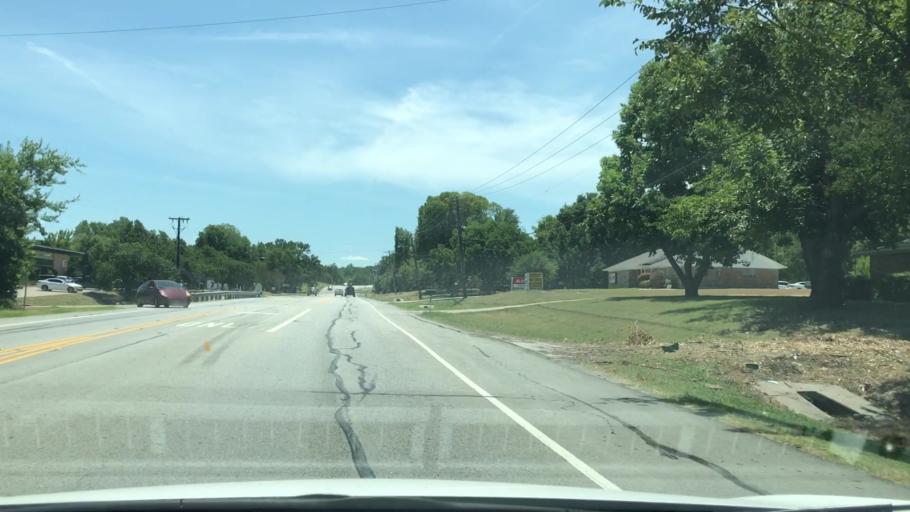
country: US
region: Texas
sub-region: Rockwall County
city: Rockwall
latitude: 32.9461
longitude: -96.4613
